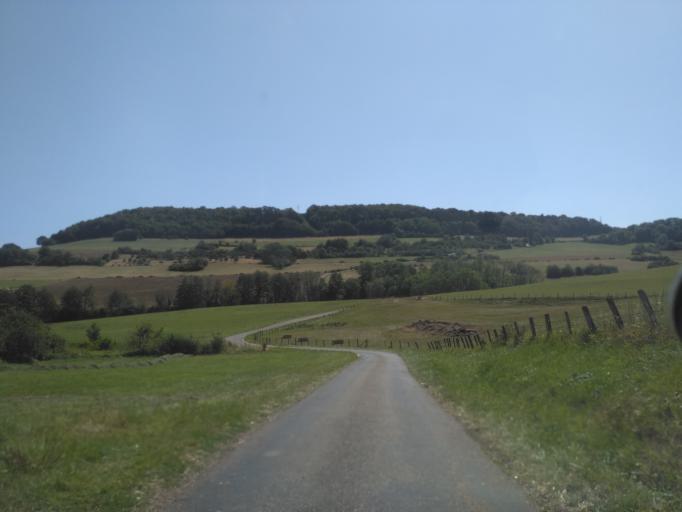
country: FR
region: Franche-Comte
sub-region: Departement de la Haute-Saone
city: Villersexel
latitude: 47.5084
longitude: 6.5185
